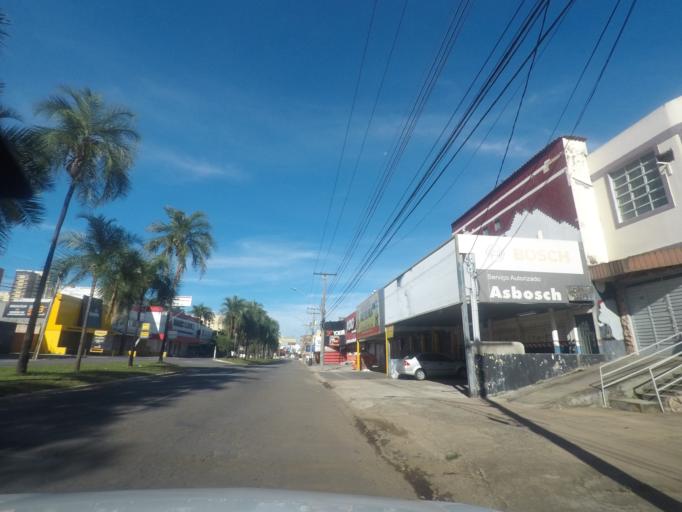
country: BR
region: Goias
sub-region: Goiania
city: Goiania
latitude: -16.6665
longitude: -49.2694
